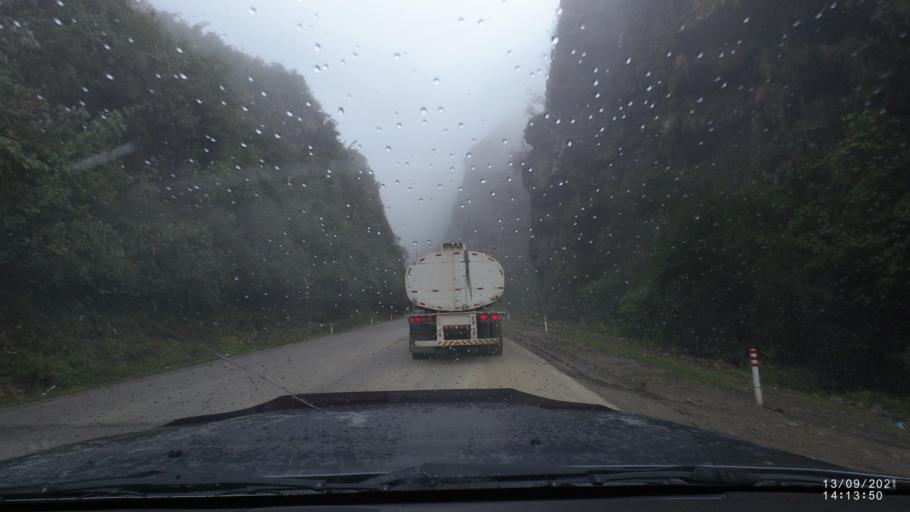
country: BO
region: Cochabamba
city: Colomi
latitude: -17.2041
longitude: -65.8910
